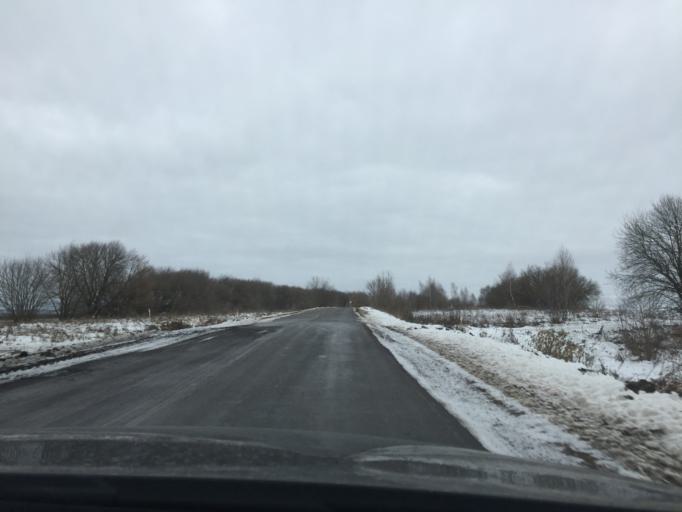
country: RU
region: Tula
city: Teploye
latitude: 53.8029
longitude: 37.5823
